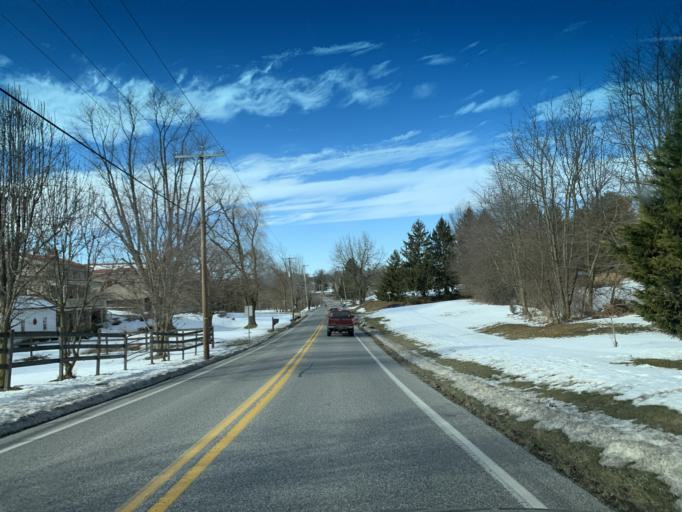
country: US
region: Pennsylvania
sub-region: York County
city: Weigelstown
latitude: 39.9557
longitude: -76.8339
